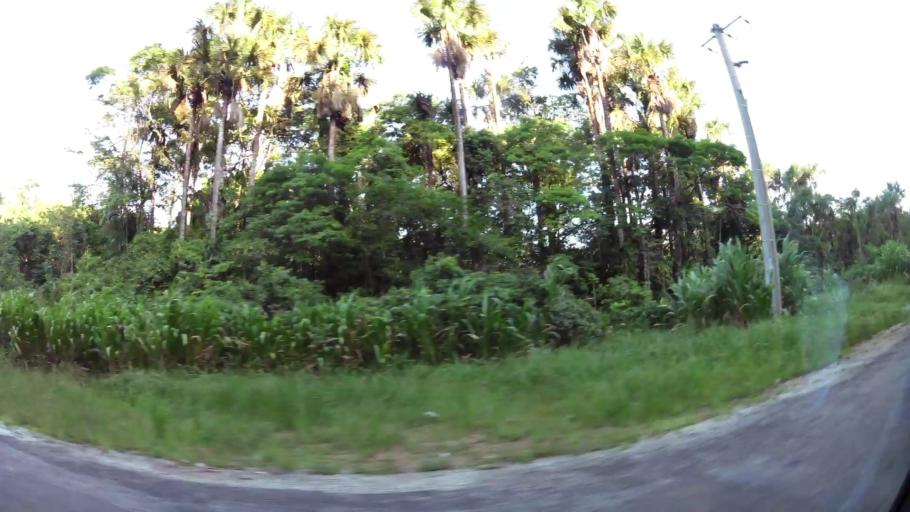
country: GF
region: Guyane
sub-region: Guyane
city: Remire-Montjoly
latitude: 4.8876
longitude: -52.2951
